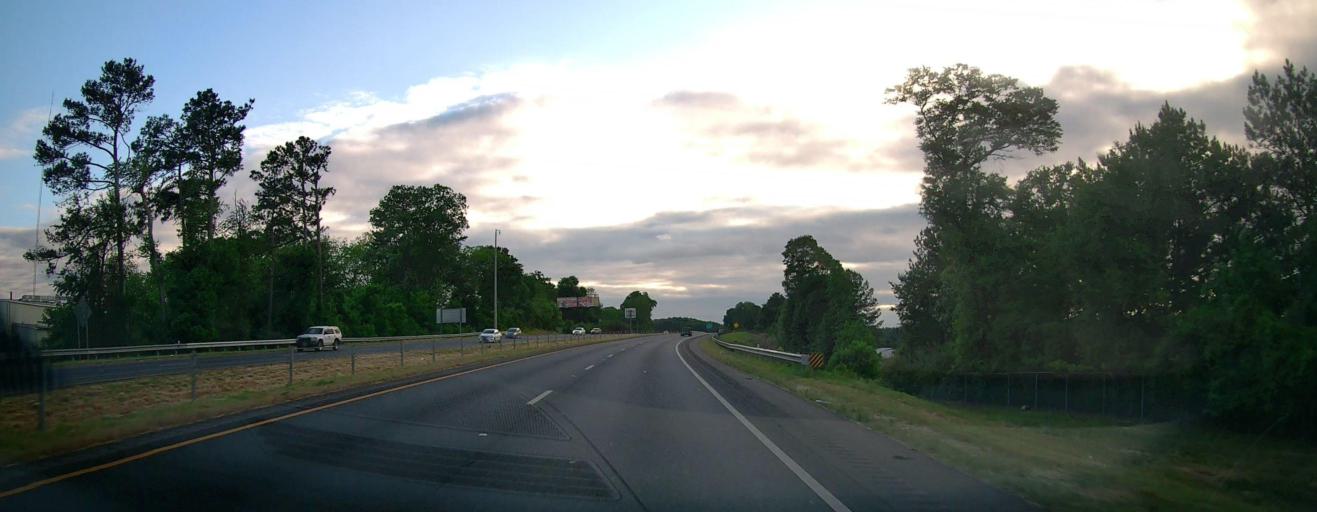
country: US
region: Georgia
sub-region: Clarke County
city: Athens
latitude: 33.9758
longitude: -83.3846
